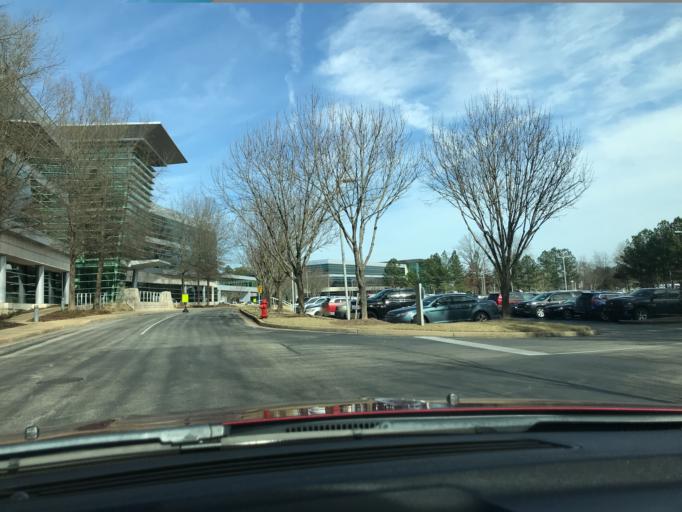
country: US
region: Tennessee
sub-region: Shelby County
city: Germantown
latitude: 35.0493
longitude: -89.7887
